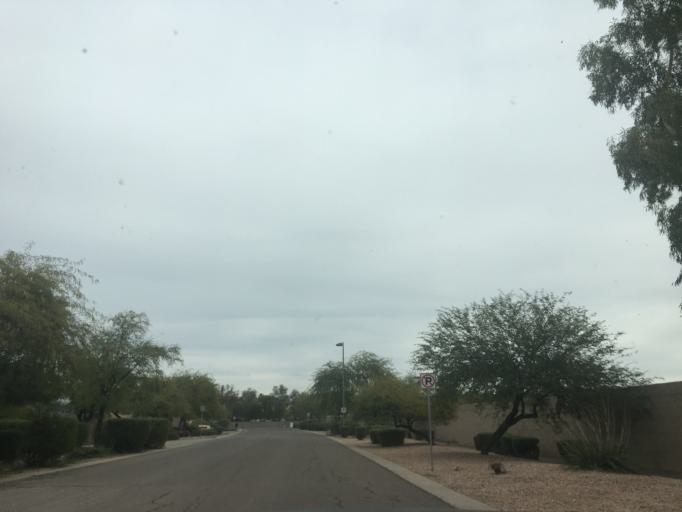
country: US
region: Arizona
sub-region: Maricopa County
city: Gilbert
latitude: 33.3530
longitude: -111.7964
